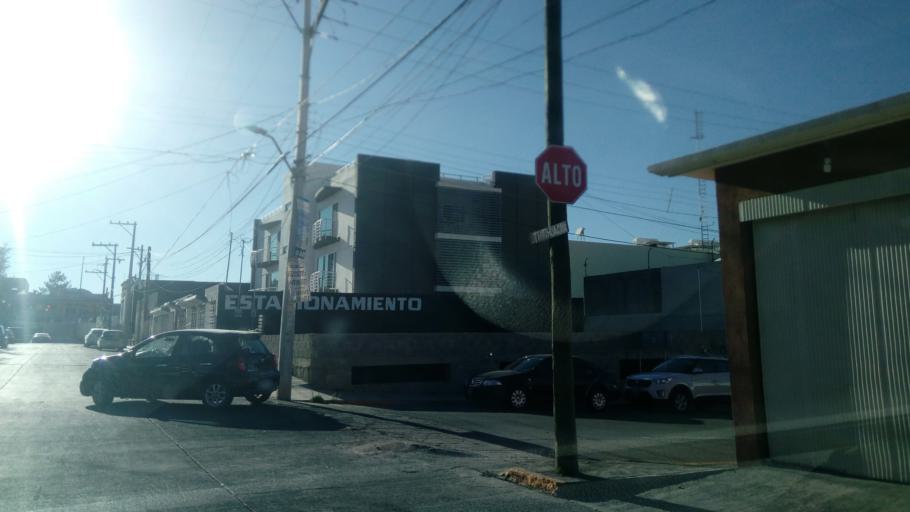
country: MX
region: Durango
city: Victoria de Durango
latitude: 24.0211
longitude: -104.6889
